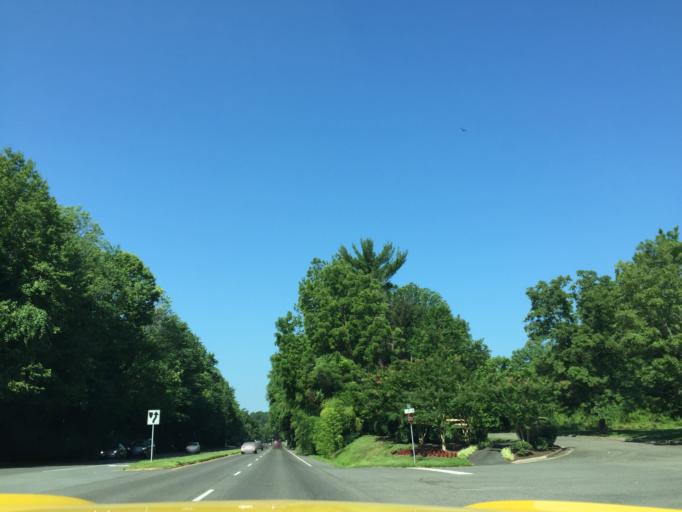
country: US
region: Virginia
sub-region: Fairfax County
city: McLean
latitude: 38.9431
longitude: -77.1545
